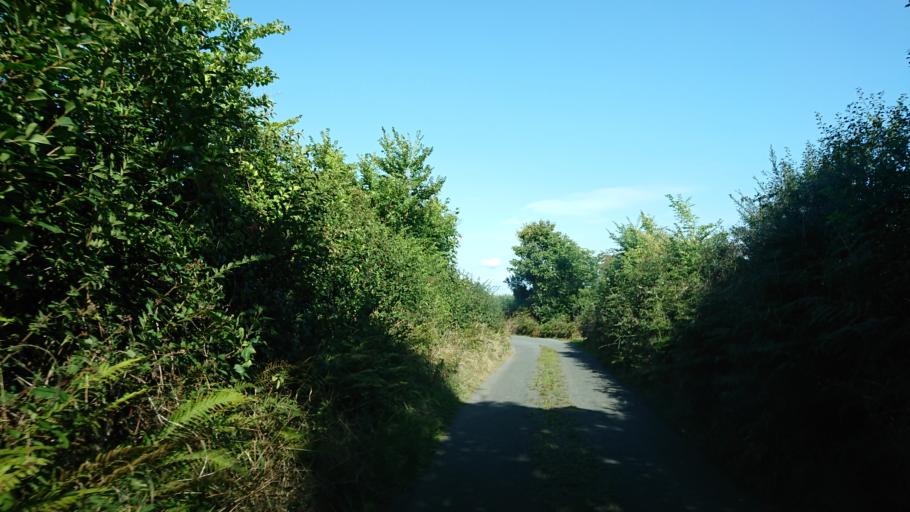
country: IE
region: Munster
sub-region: Waterford
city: Waterford
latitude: 52.2062
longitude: -7.0574
